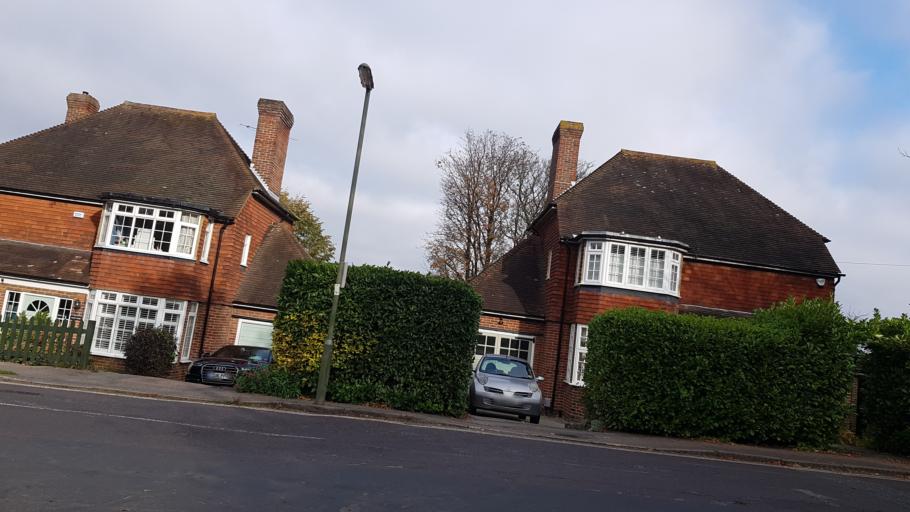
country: GB
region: England
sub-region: Surrey
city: Guildford
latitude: 51.2317
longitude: -0.6018
